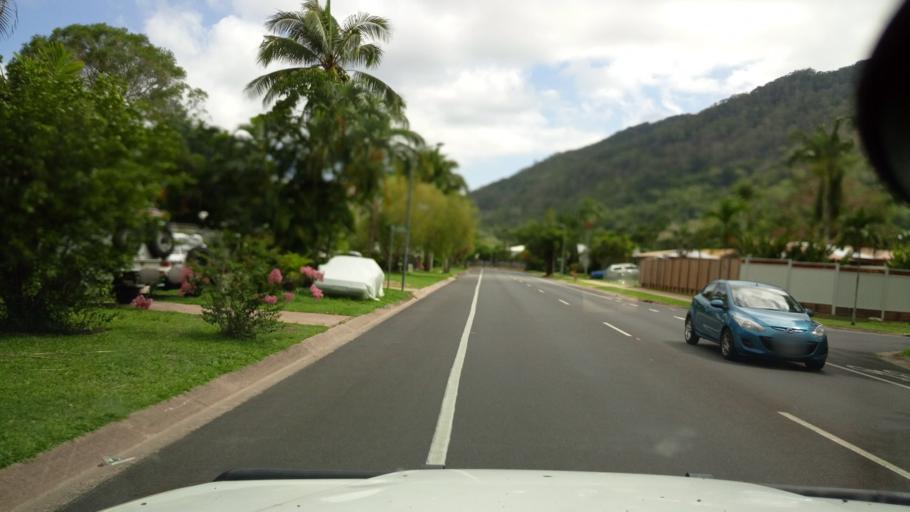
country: AU
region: Queensland
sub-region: Cairns
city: Redlynch
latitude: -16.9158
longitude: 145.7211
